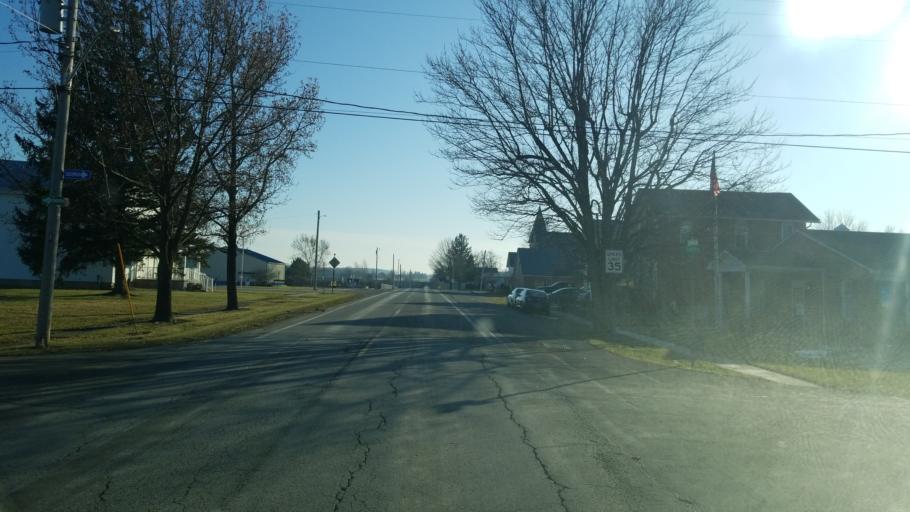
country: US
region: Ohio
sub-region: Sandusky County
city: Green Springs
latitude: 41.1225
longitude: -83.0155
